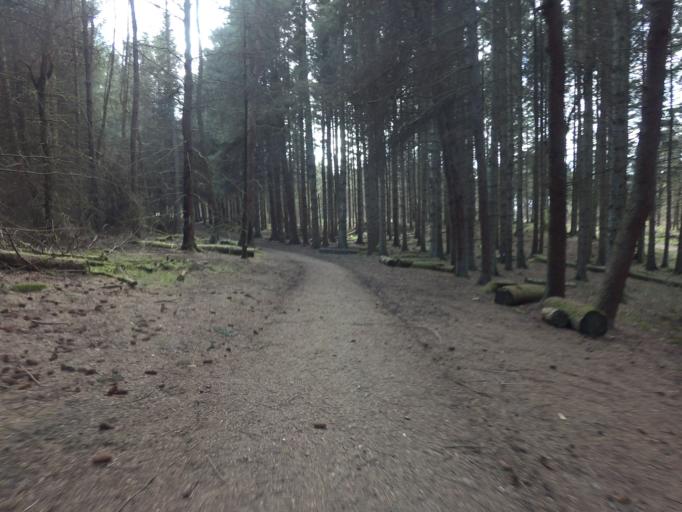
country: GB
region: Scotland
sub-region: West Lothian
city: Livingston
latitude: 55.9152
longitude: -3.5472
